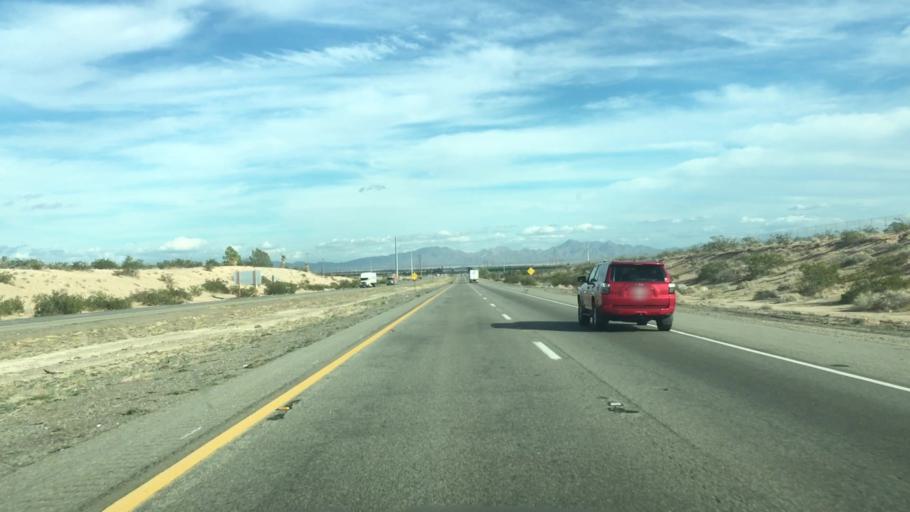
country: US
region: California
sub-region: Riverside County
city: Mesa Verde
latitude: 33.6064
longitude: -114.7055
